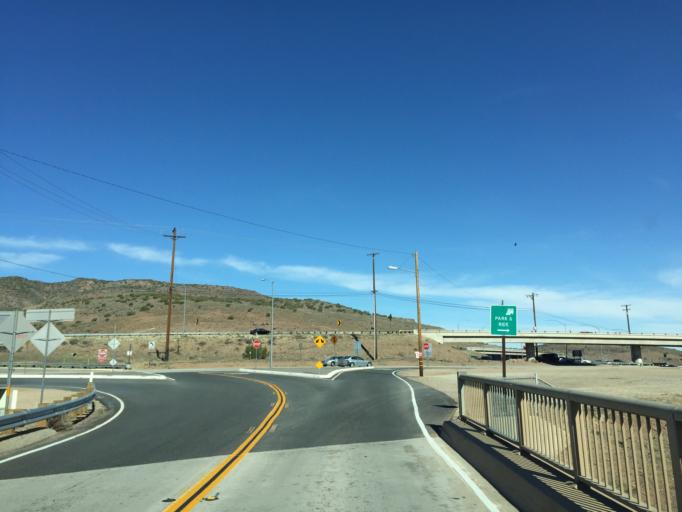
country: US
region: California
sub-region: Los Angeles County
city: Vincent
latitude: 34.5087
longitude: -118.1107
